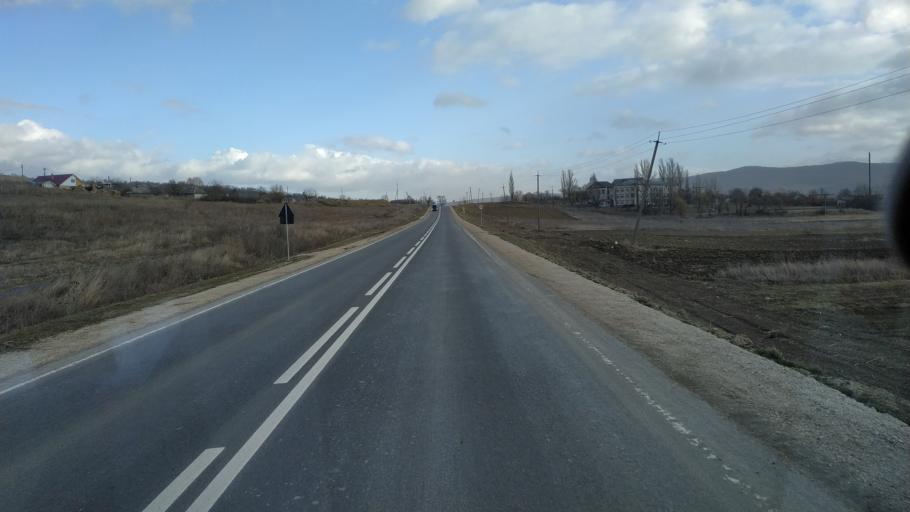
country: MD
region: Calarasi
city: Calarasi
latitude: 47.3253
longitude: 28.1027
